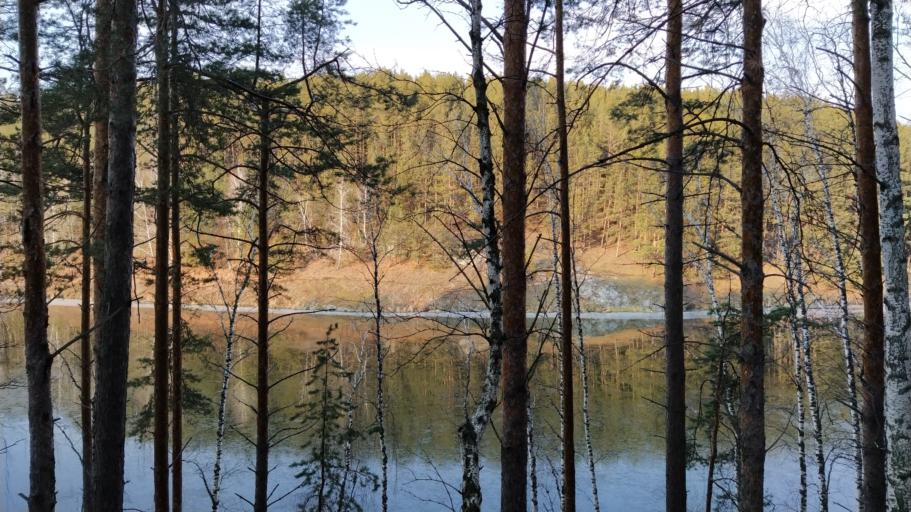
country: RU
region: Sverdlovsk
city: Martyush
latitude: 56.4045
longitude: 61.8712
